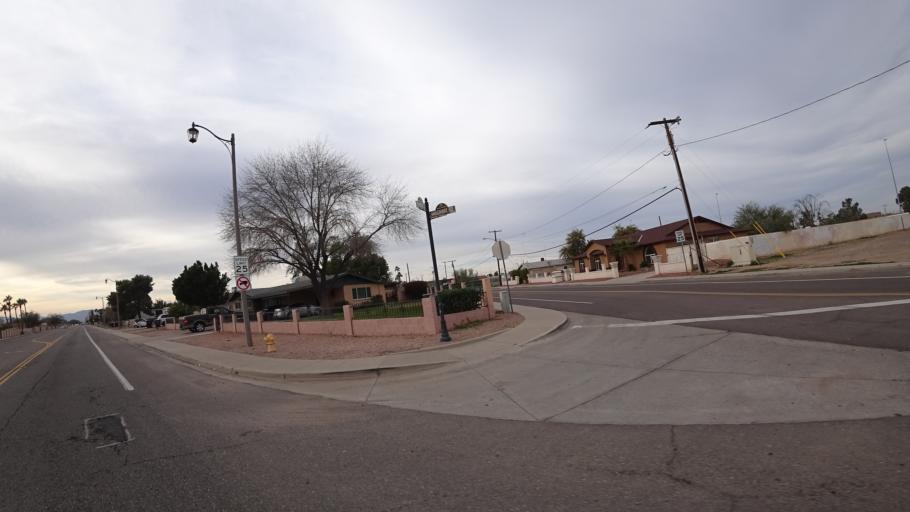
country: US
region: Arizona
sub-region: Maricopa County
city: Surprise
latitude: 33.6236
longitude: -112.3329
